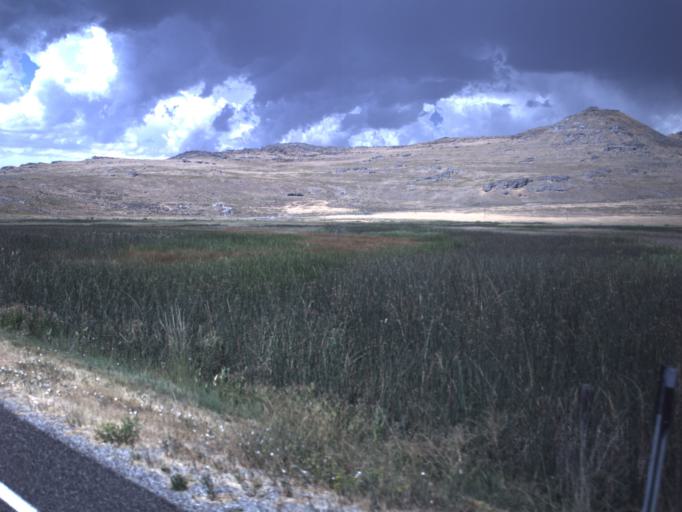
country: US
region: Utah
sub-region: Box Elder County
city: Tremonton
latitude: 41.6118
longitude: -112.3577
